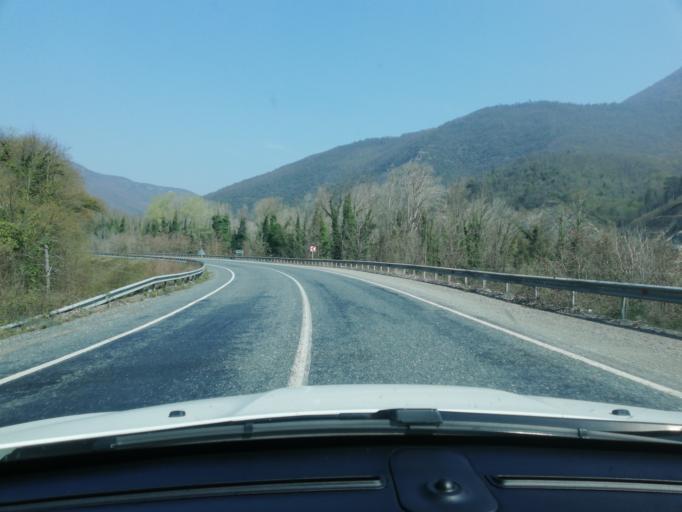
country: TR
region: Zonguldak
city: Gokcebey
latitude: 41.2520
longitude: 32.1631
